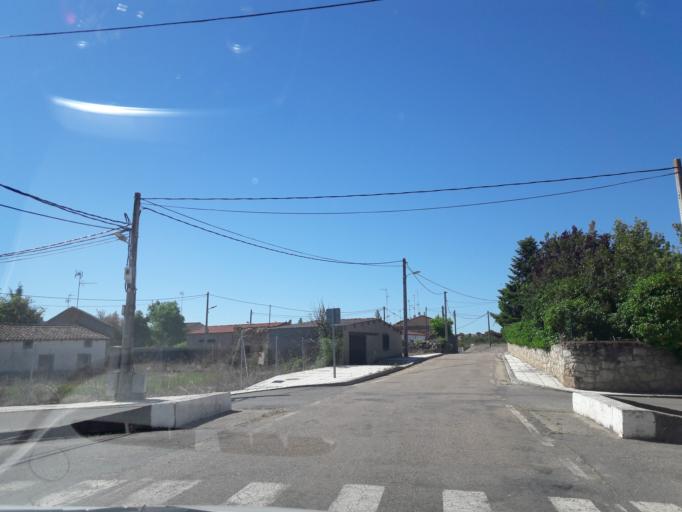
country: ES
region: Castille and Leon
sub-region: Provincia de Salamanca
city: Zarapicos
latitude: 41.0383
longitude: -5.8450
